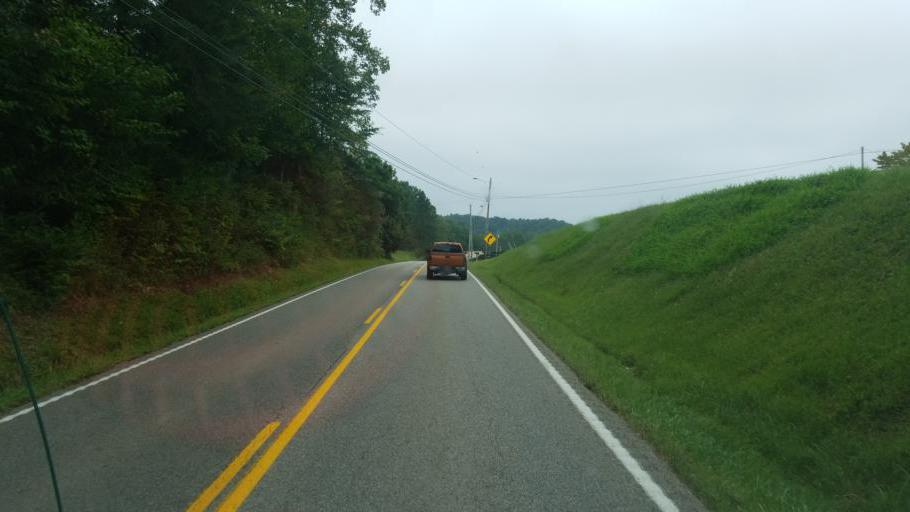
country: US
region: Kentucky
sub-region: Rowan County
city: Morehead
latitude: 38.2271
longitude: -83.4647
